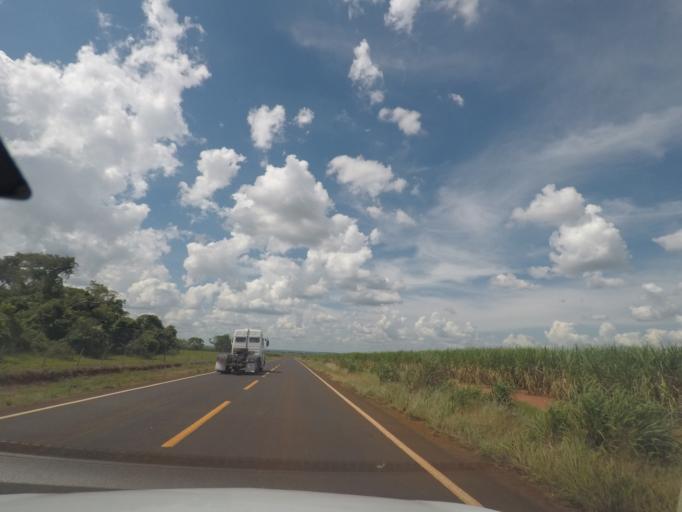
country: BR
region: Minas Gerais
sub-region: Conceicao Das Alagoas
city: Conceicao das Alagoas
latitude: -19.8471
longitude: -48.5959
